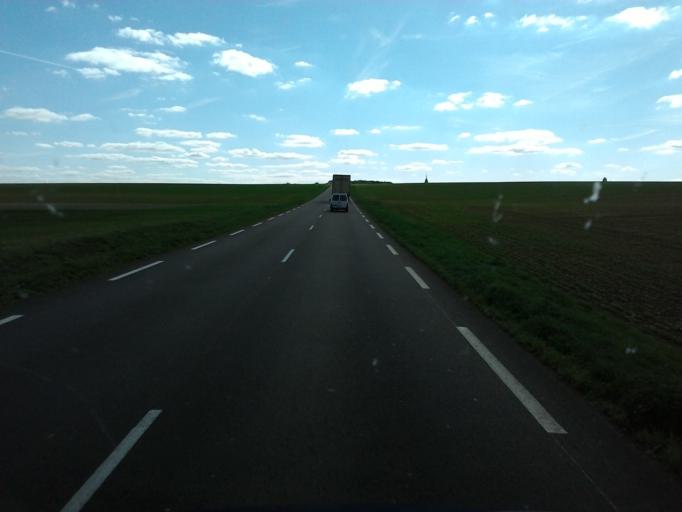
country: FR
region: Bourgogne
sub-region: Departement de la Cote-d'Or
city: Chatillon-sur-Seine
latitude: 47.7625
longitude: 4.5012
